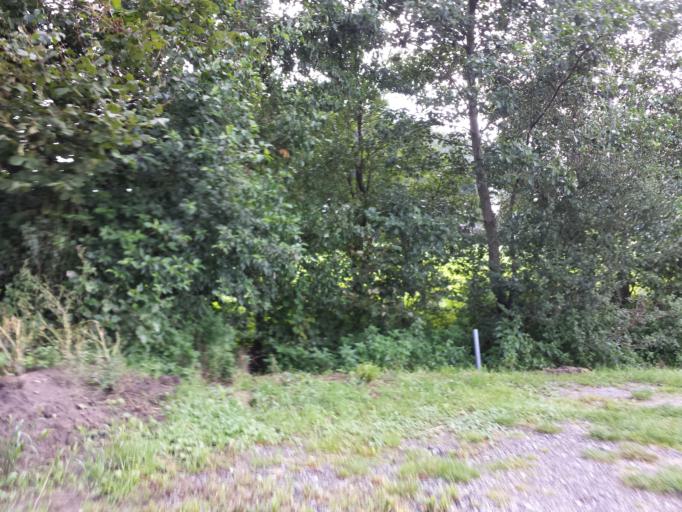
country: DE
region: North Rhine-Westphalia
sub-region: Regierungsbezirk Detmold
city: Delbruck
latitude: 51.7871
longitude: 8.4989
